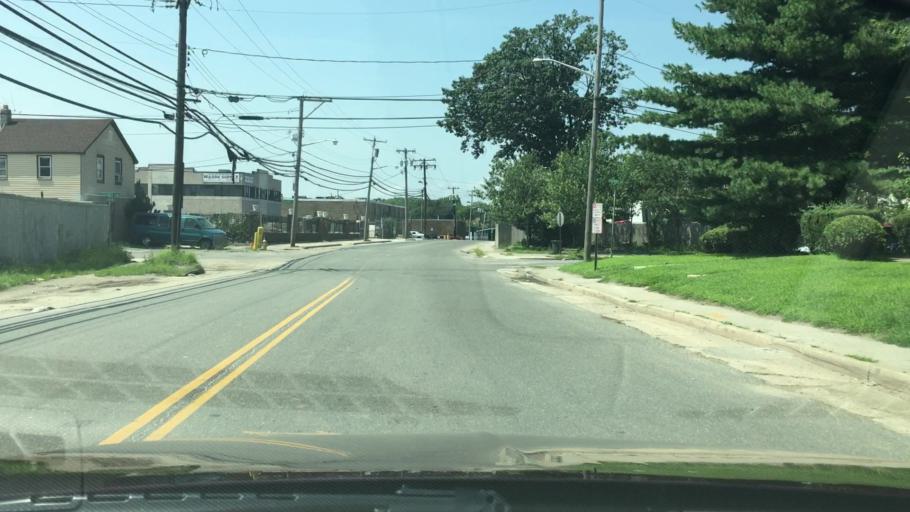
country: US
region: New York
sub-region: Nassau County
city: New Cassel
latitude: 40.7571
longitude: -73.5759
